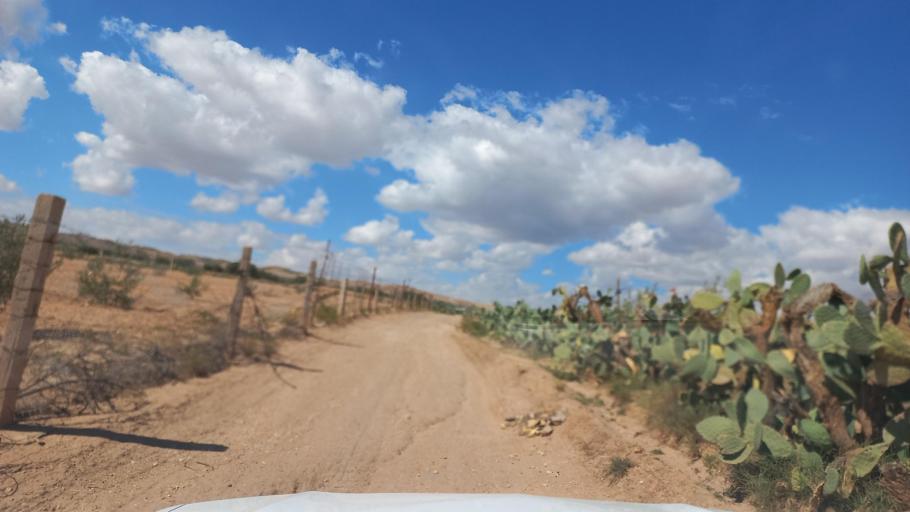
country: TN
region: Al Qasrayn
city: Sbiba
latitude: 35.3542
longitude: 9.0190
